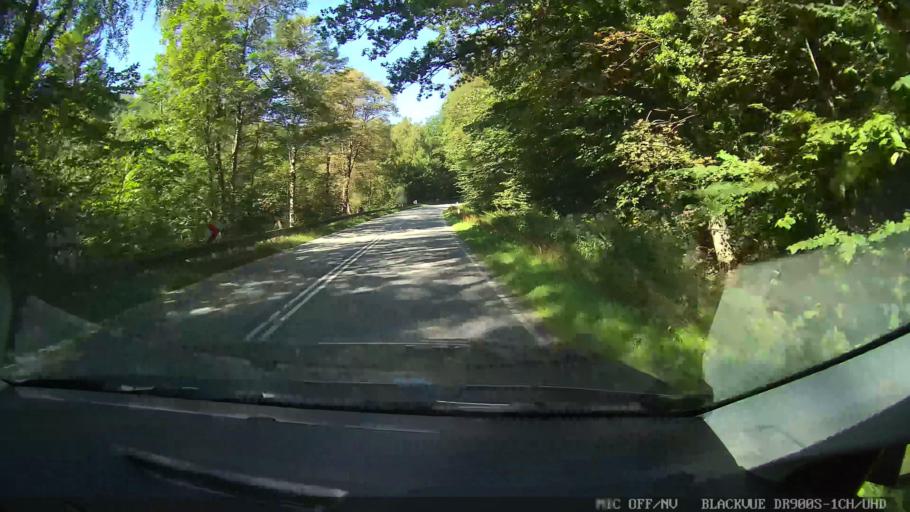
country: DK
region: North Denmark
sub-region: Mariagerfjord Kommune
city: Mariager
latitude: 56.6066
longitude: 9.9970
